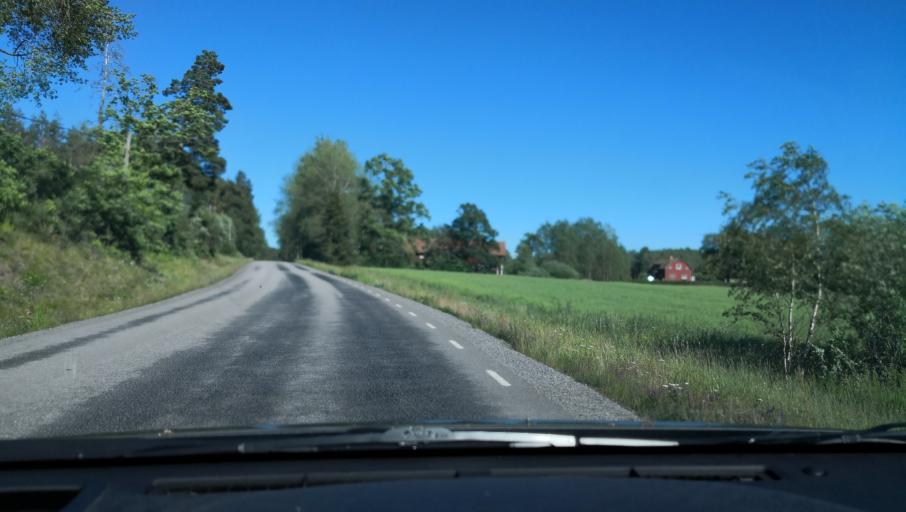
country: SE
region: Soedermanland
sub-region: Eskilstuna Kommun
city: Arla
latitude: 59.3231
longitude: 16.6202
